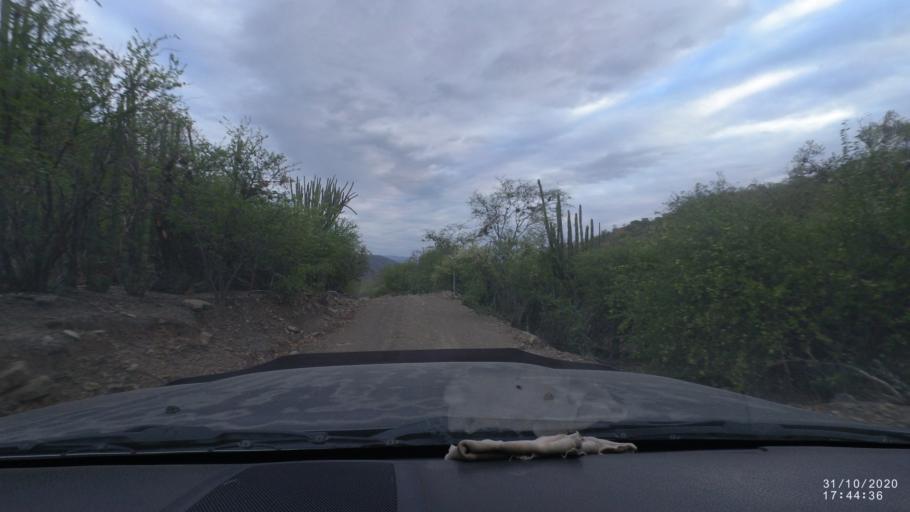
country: BO
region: Chuquisaca
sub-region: Provincia Zudanez
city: Mojocoya
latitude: -18.6112
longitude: -64.5468
